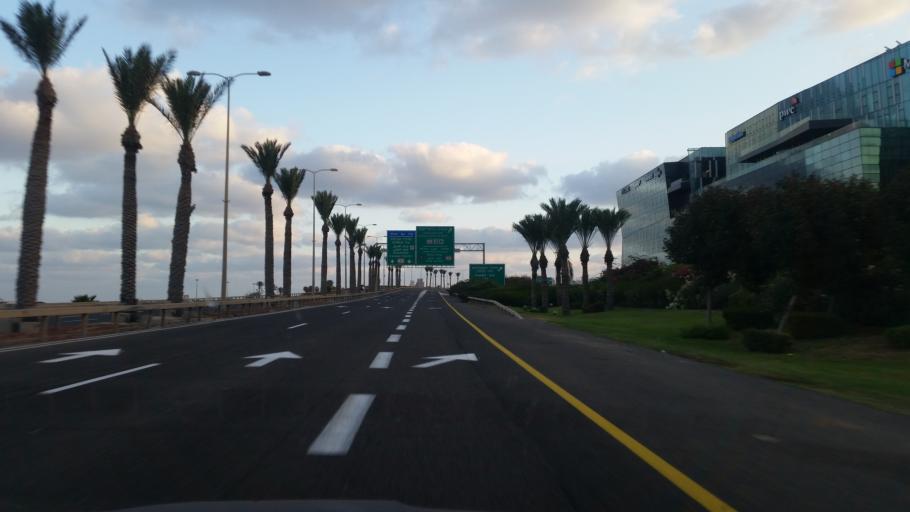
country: IL
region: Haifa
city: Tirat Karmel
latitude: 32.7867
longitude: 34.9567
